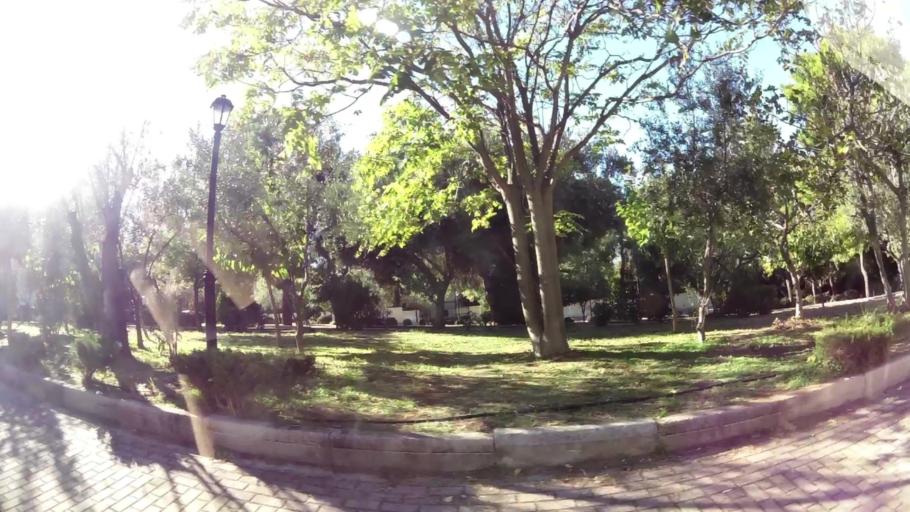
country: GR
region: Attica
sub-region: Nomarchia Athinas
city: Nea Erythraia
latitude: 38.0960
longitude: 23.8193
